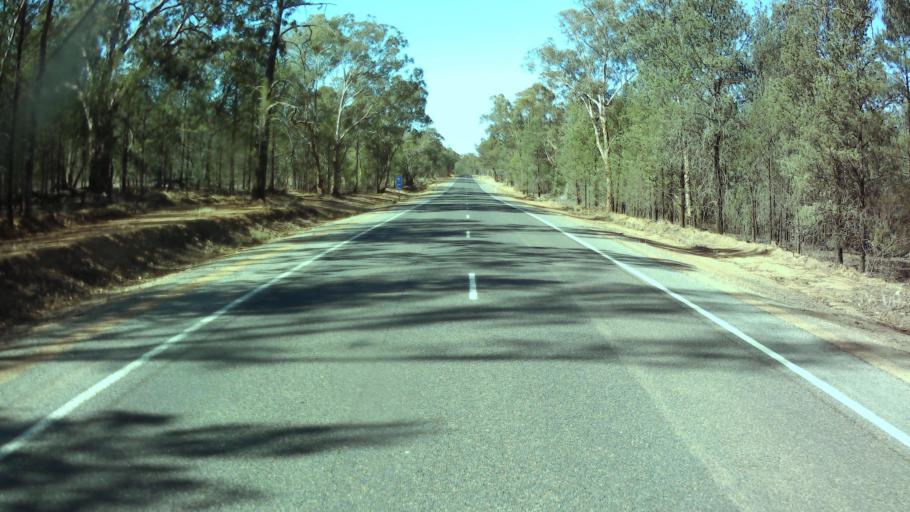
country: AU
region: New South Wales
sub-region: Weddin
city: Grenfell
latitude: -33.7499
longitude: 148.0855
